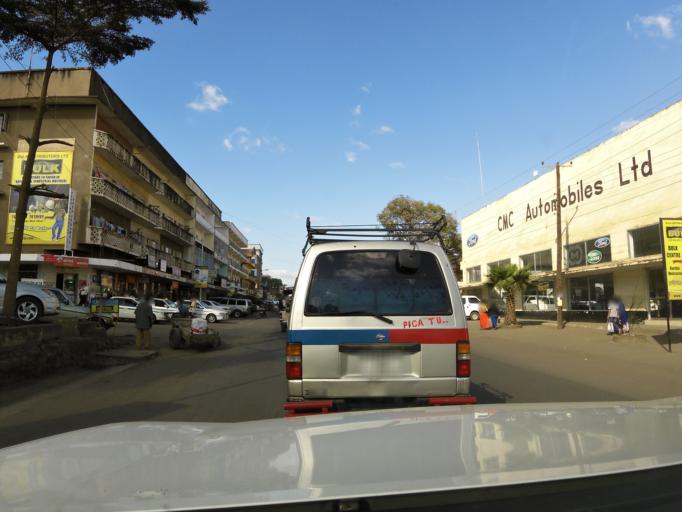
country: TZ
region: Arusha
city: Arusha
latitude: -3.3746
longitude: 36.6812
